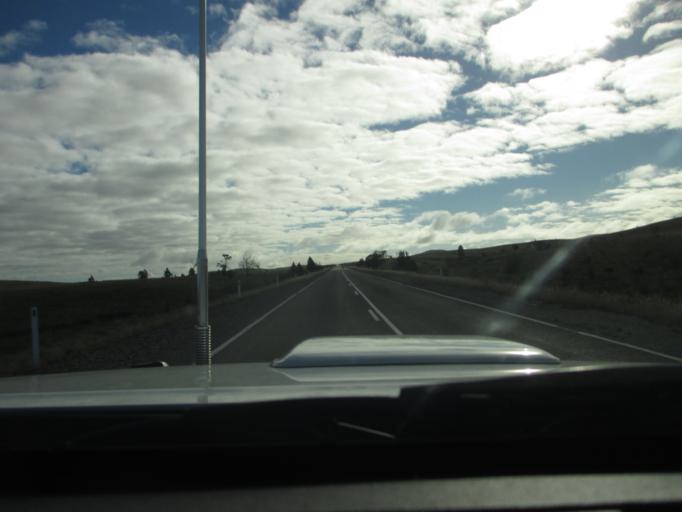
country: AU
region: South Australia
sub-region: Peterborough
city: Peterborough
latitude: -32.5855
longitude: 138.5604
